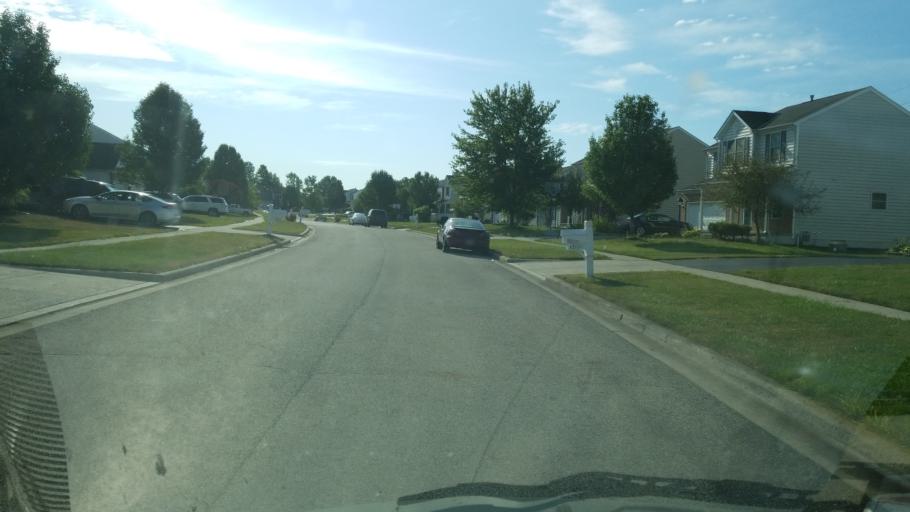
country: US
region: Ohio
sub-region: Delaware County
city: Lewis Center
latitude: 40.1777
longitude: -83.0028
